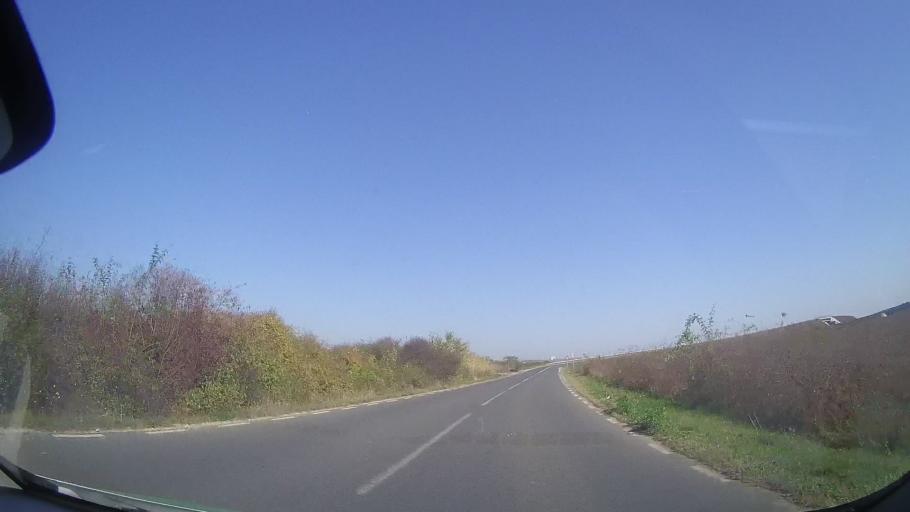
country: RO
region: Timis
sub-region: Comuna Balint
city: Balint
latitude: 45.7861
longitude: 21.8481
